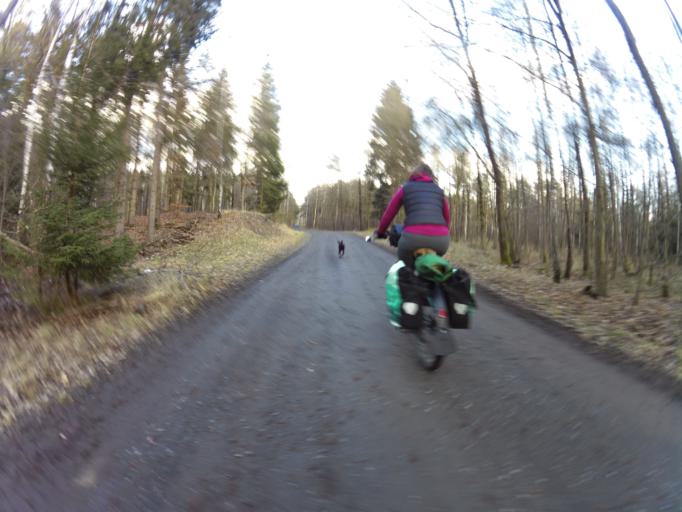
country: PL
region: West Pomeranian Voivodeship
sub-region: Powiat mysliborski
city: Debno
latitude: 52.7646
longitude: 14.7260
